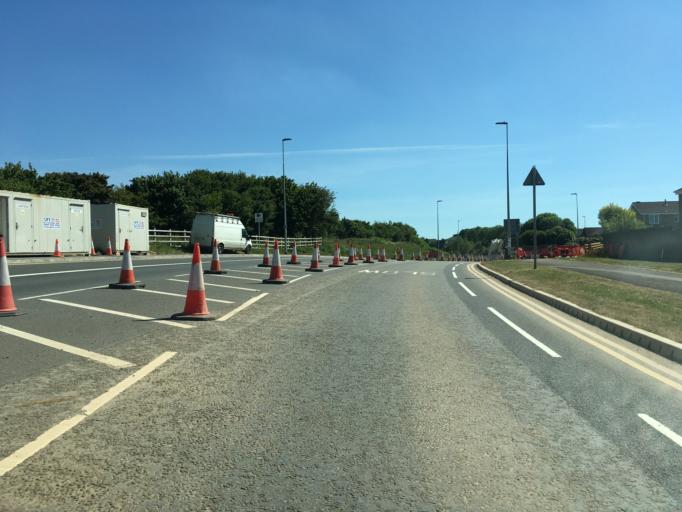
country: GB
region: England
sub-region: South Gloucestershire
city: Stoke Gifford
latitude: 51.5232
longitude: -2.5308
